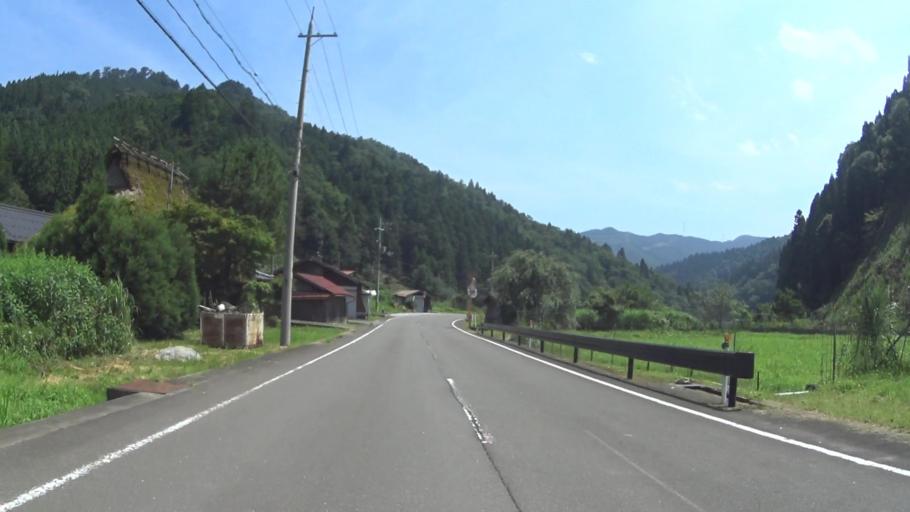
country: JP
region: Kyoto
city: Maizuru
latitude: 35.3407
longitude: 135.5335
